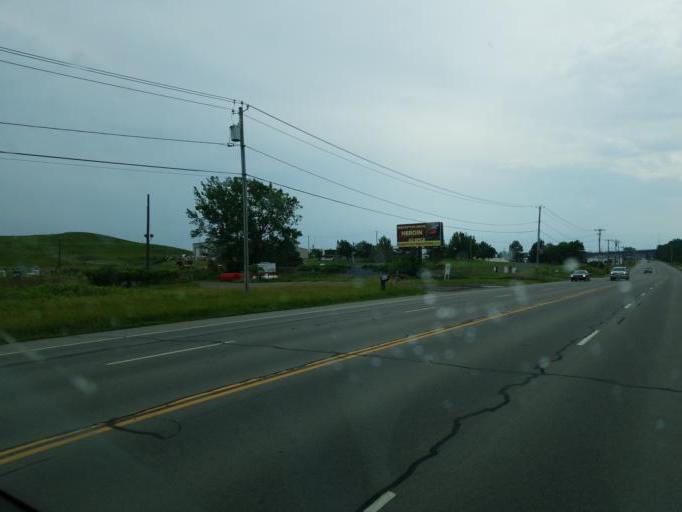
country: US
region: New York
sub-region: Erie County
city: Grandyle Village
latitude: 43.0023
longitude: -78.9245
